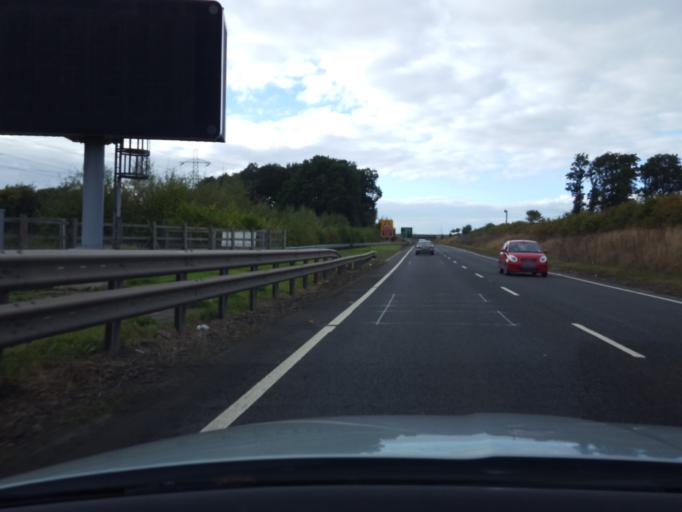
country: GB
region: Scotland
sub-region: Midlothian
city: Dalkeith
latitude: 55.9122
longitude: -3.0556
